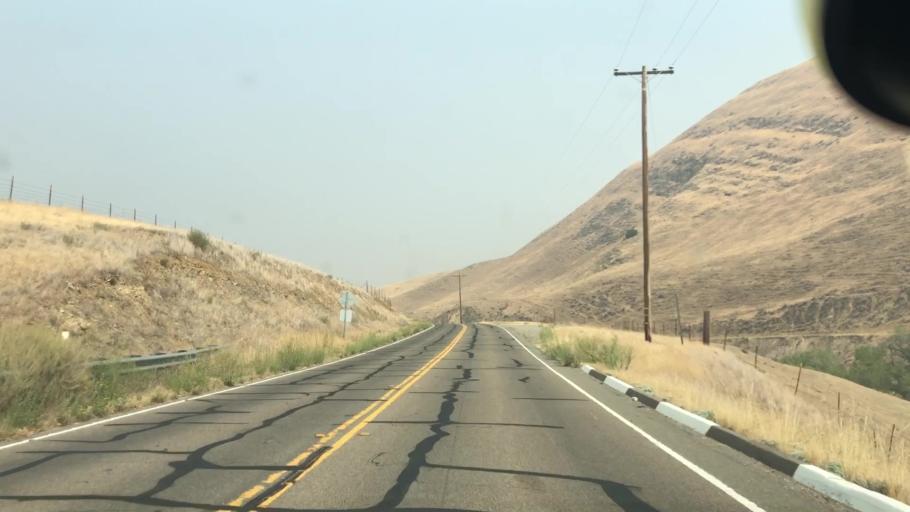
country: US
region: California
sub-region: San Joaquin County
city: Tracy
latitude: 37.6569
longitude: -121.4831
